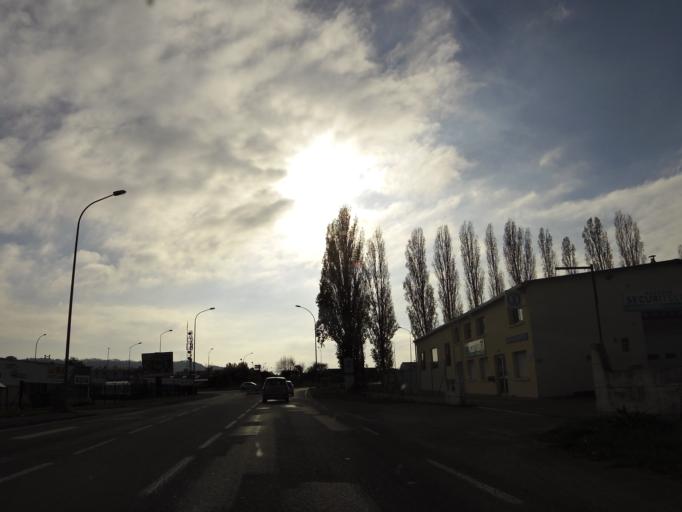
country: FR
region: Rhone-Alpes
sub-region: Departement de l'Ain
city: Amberieu-en-Bugey
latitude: 45.9663
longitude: 5.3382
